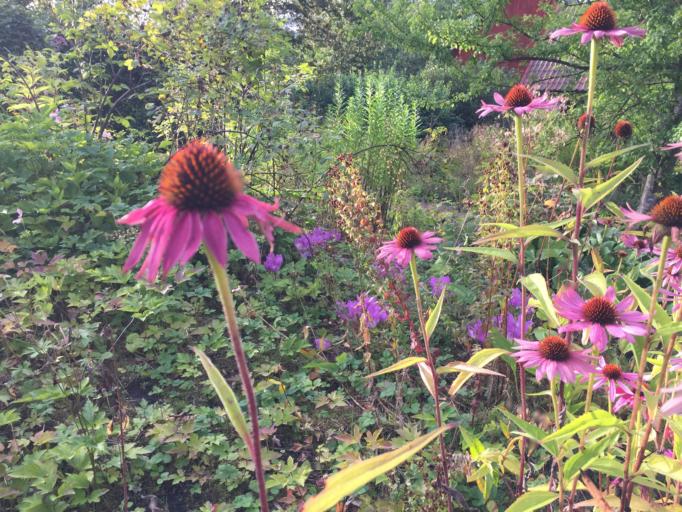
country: SE
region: Skane
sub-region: Perstorps Kommun
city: Perstorp
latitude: 56.2136
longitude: 13.3398
